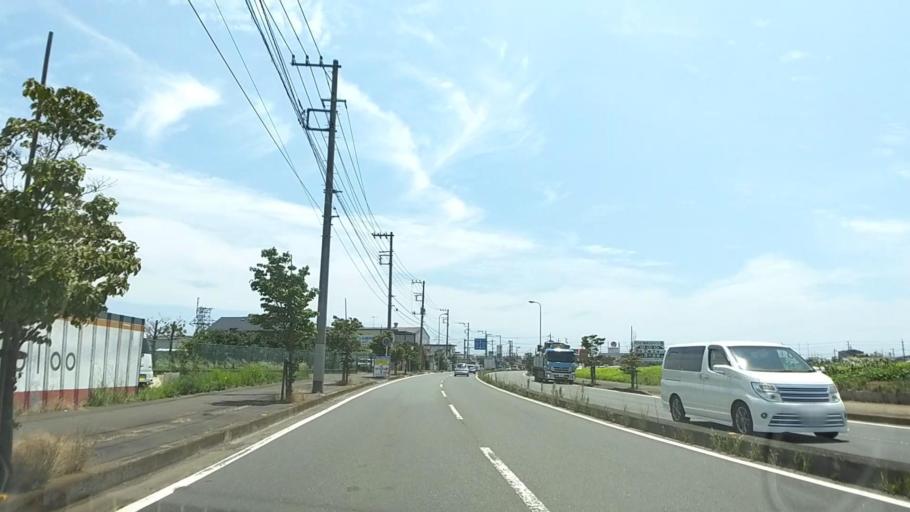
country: JP
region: Kanagawa
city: Atsugi
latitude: 35.4091
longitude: 139.3830
